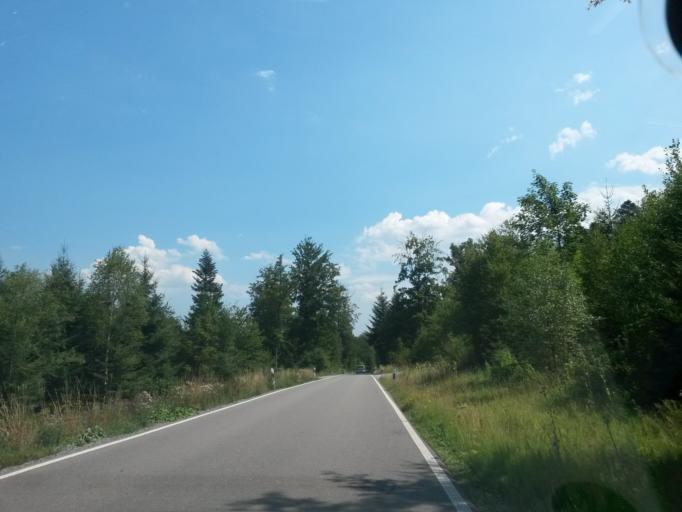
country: DE
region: Baden-Wuerttemberg
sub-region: Karlsruhe Region
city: Neuenburg
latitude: 48.8336
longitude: 8.5595
